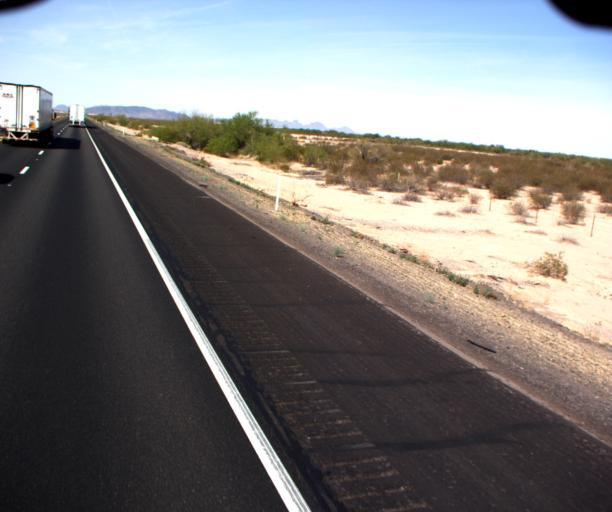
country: US
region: Arizona
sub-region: La Paz County
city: Salome
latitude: 33.6259
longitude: -113.7309
